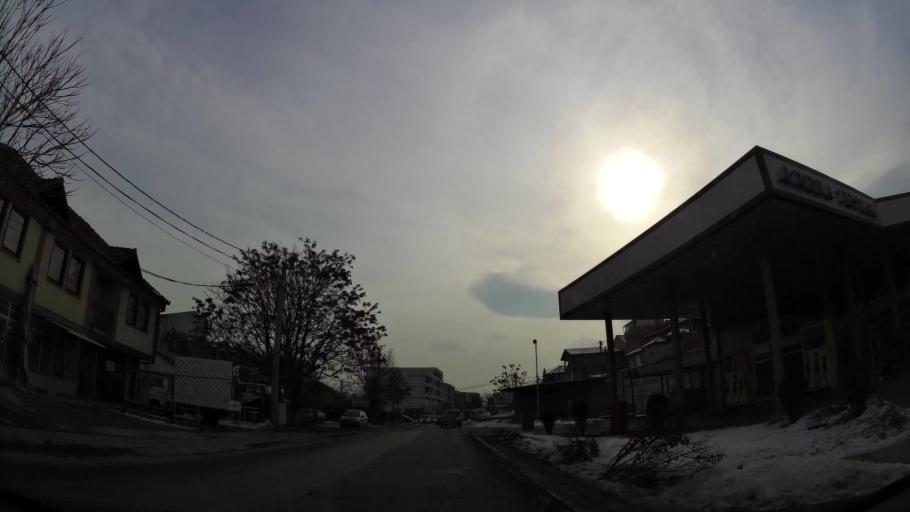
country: MK
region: Cair
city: Cair
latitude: 42.0116
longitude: 21.4324
